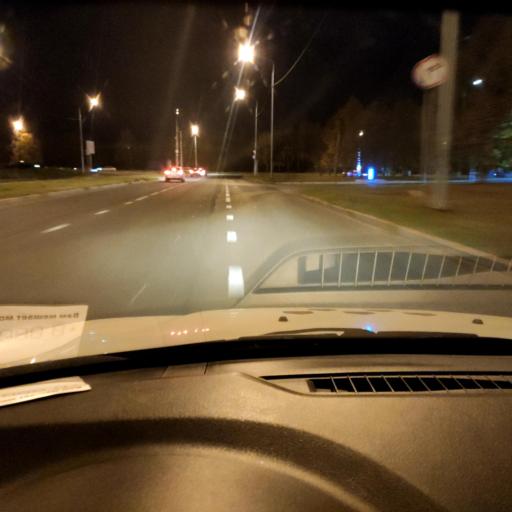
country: RU
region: Samara
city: Tol'yatti
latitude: 53.5014
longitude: 49.2693
